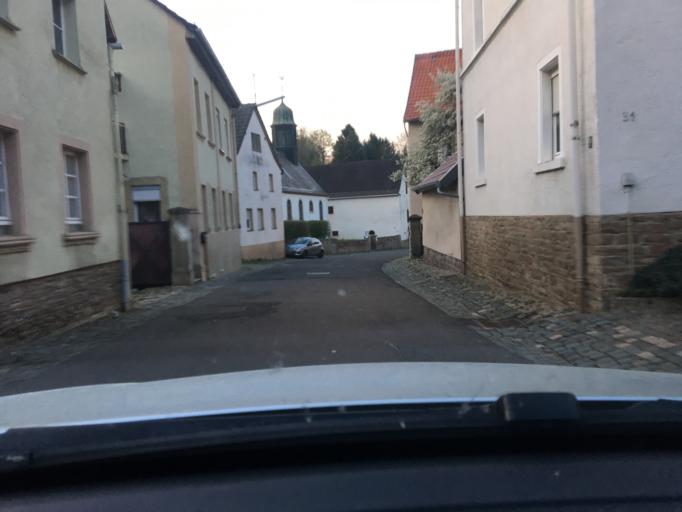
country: DE
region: Rheinland-Pfalz
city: Kalkofen
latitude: 49.7321
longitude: 7.8353
